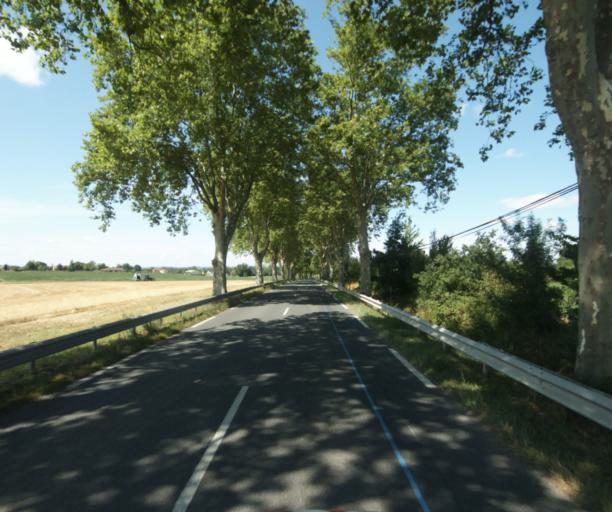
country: FR
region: Midi-Pyrenees
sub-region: Departement de la Haute-Garonne
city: Revel
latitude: 43.4800
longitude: 2.0147
